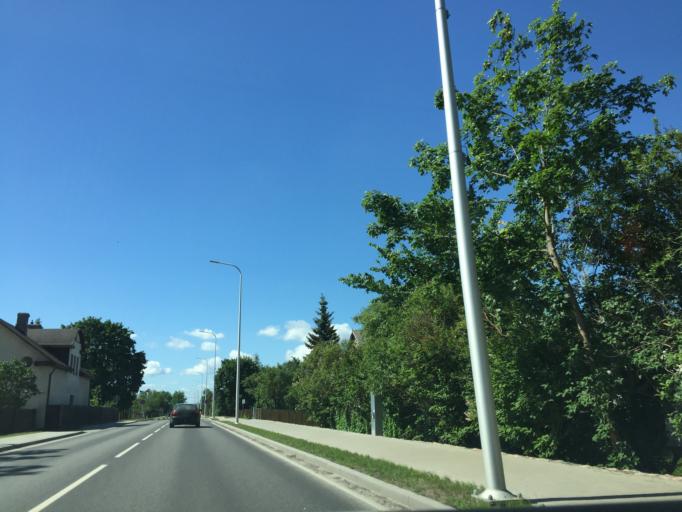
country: LV
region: Marupe
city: Marupe
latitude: 56.9087
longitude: 24.0602
